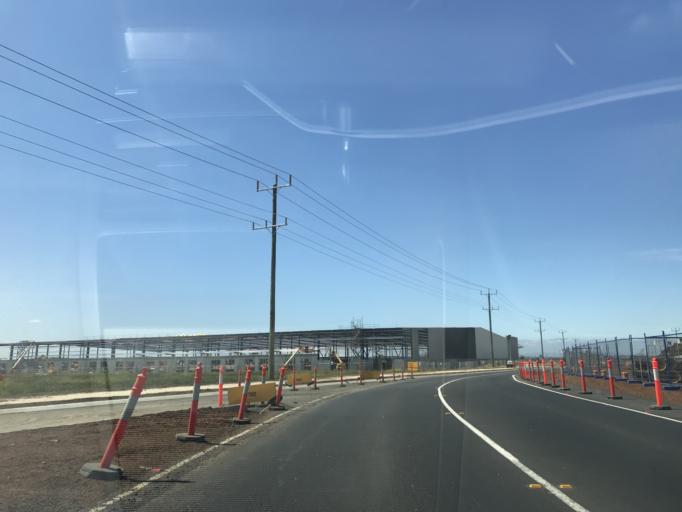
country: AU
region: Victoria
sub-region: Wyndham
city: Truganina
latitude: -37.8393
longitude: 144.7506
